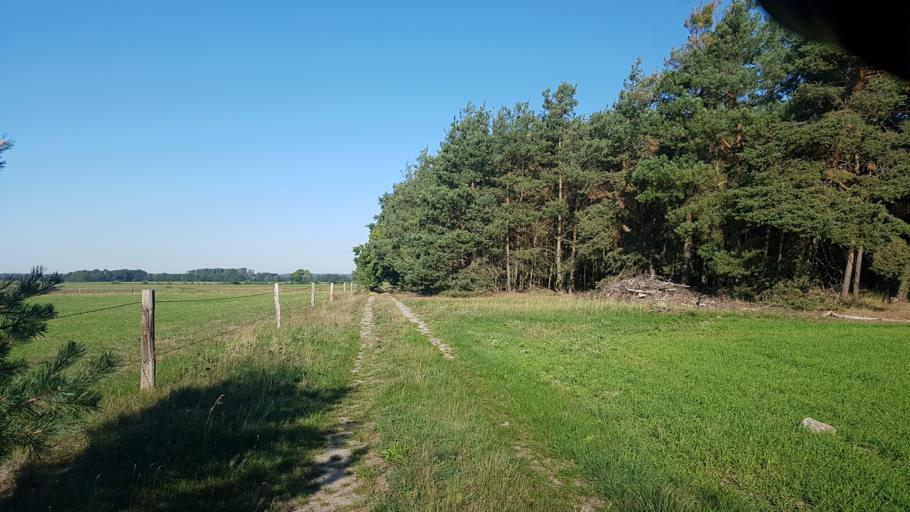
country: DE
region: Brandenburg
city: Ruckersdorf
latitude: 51.5831
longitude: 13.5554
